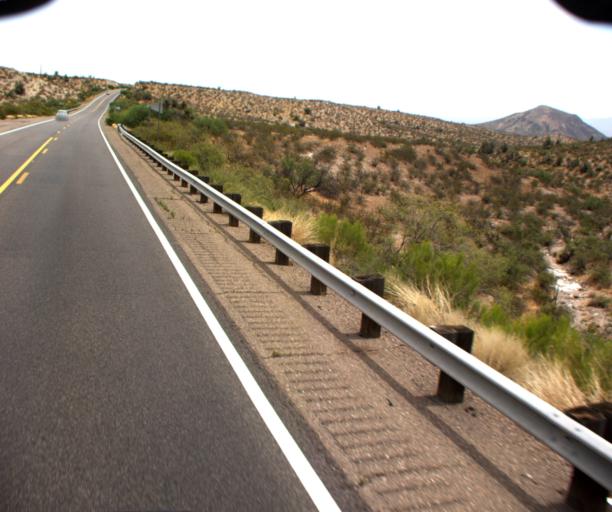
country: US
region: Arizona
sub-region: Gila County
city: Peridot
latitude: 33.2841
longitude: -110.3444
